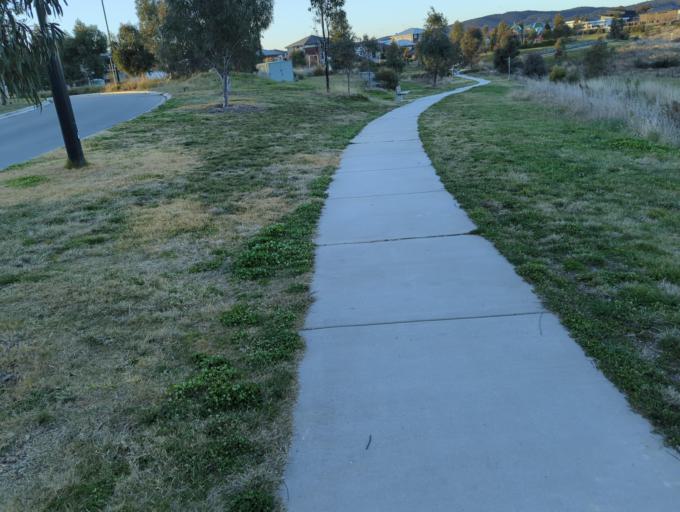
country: AU
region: New South Wales
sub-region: Queanbeyan
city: Queanbeyan
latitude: -35.4254
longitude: 149.2443
